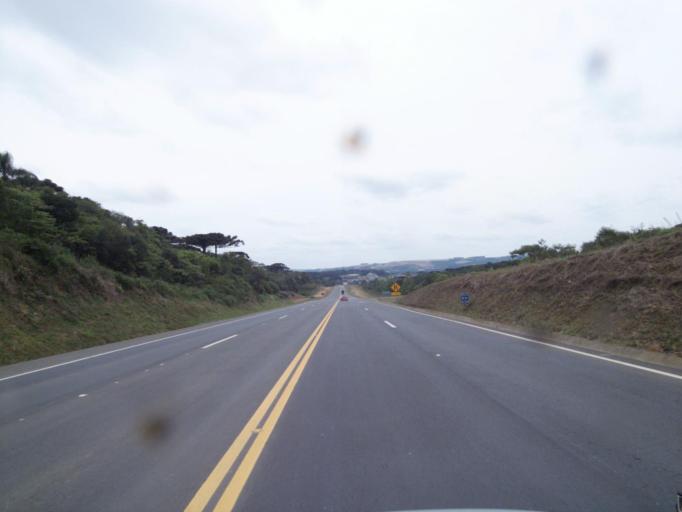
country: BR
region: Parana
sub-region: Irati
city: Irati
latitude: -25.4629
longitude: -50.5942
